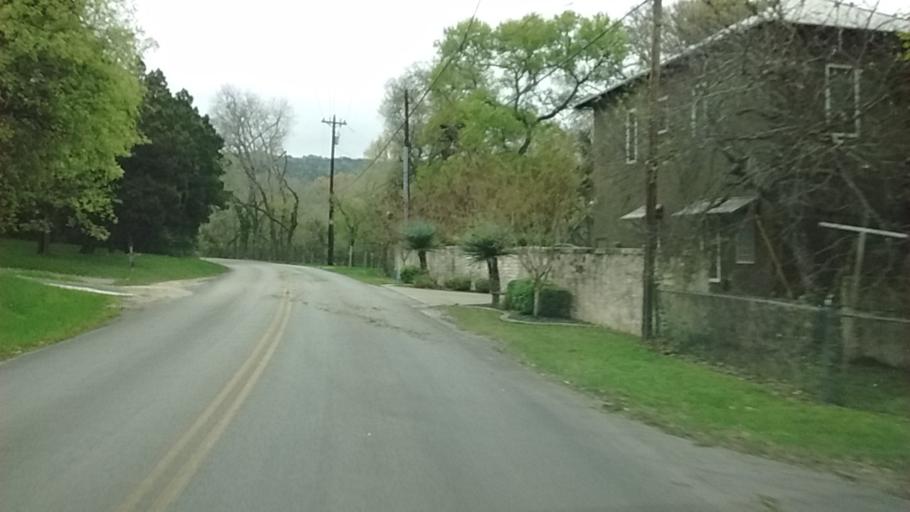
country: US
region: Texas
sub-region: Comal County
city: New Braunfels
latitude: 29.8022
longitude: -98.1480
